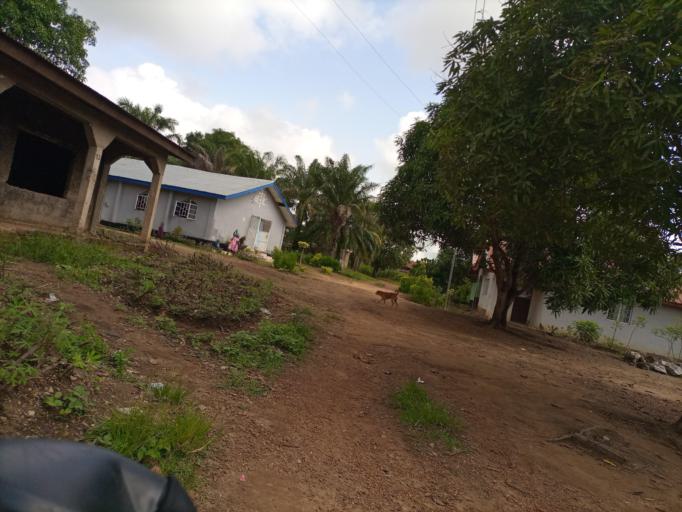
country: SL
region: Southern Province
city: Bo
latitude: 7.9681
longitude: -11.7622
